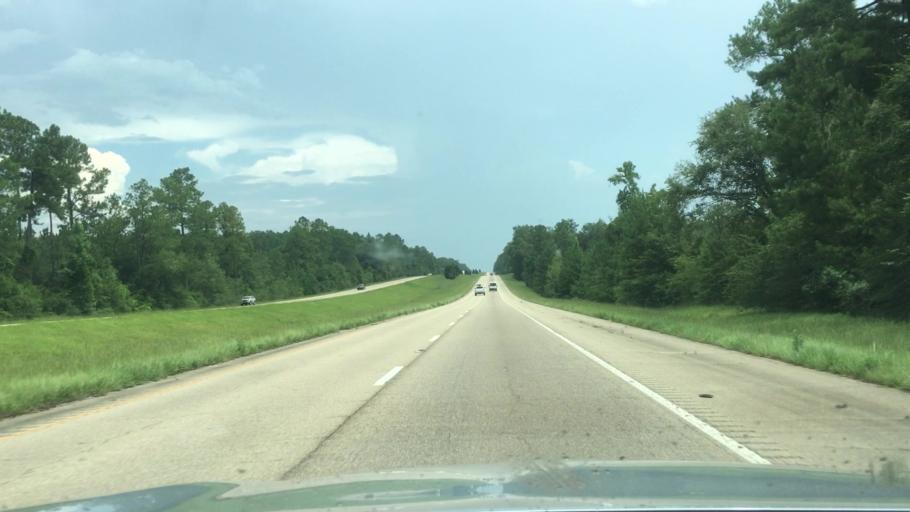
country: US
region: Mississippi
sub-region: Lamar County
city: Lumberton
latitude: 30.9441
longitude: -89.4474
